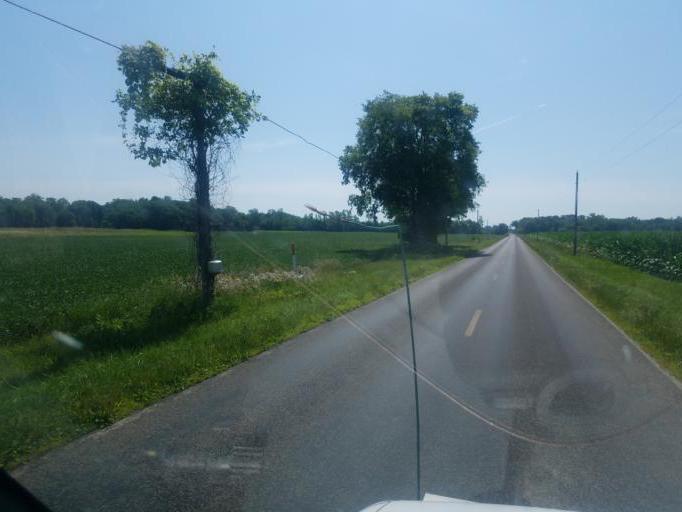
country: US
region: Ohio
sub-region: Champaign County
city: North Lewisburg
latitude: 40.2140
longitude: -83.5049
